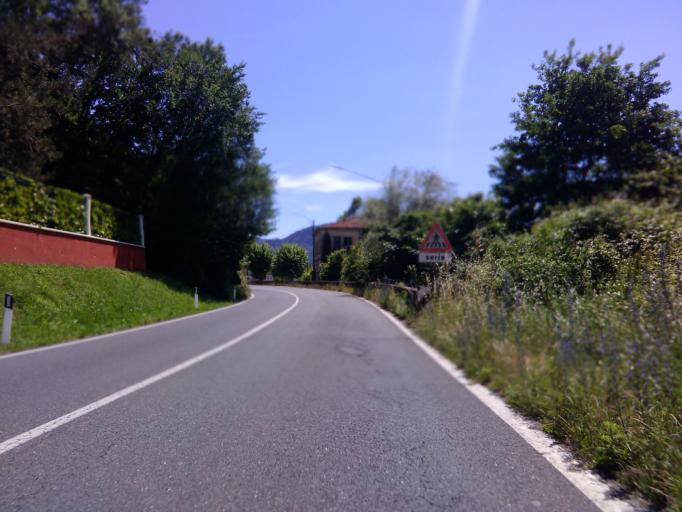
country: IT
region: Tuscany
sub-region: Provincia di Massa-Carrara
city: Terrarossa
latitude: 44.2326
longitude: 9.9605
